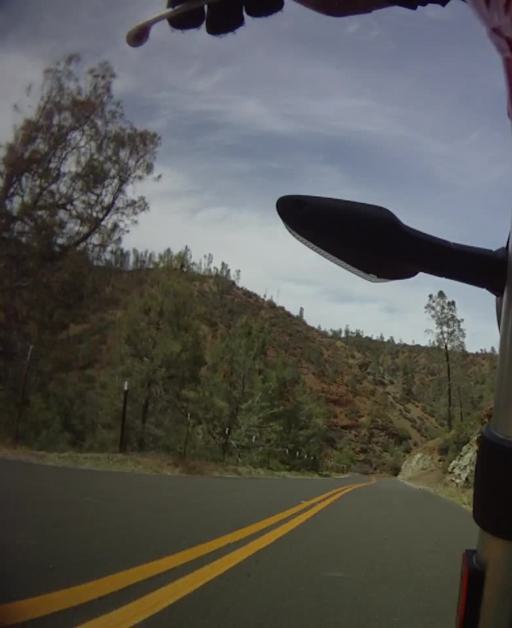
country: US
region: California
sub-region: Stanislaus County
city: Patterson
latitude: 37.4094
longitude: -121.4289
